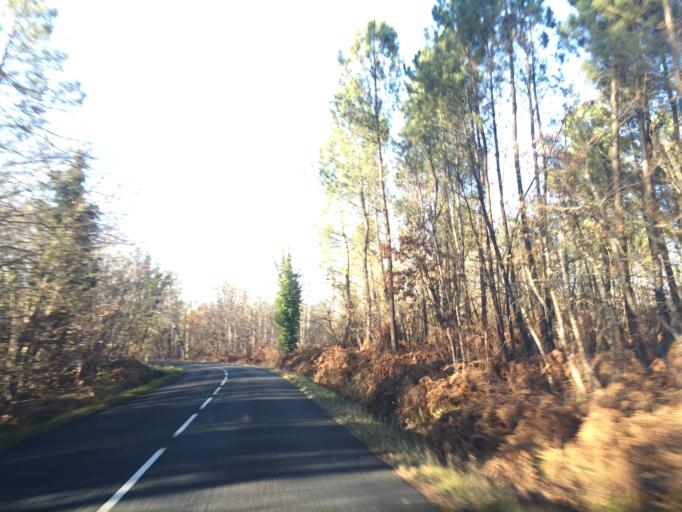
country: FR
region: Aquitaine
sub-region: Departement de la Dordogne
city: Neuvic
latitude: 45.1453
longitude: 0.4341
